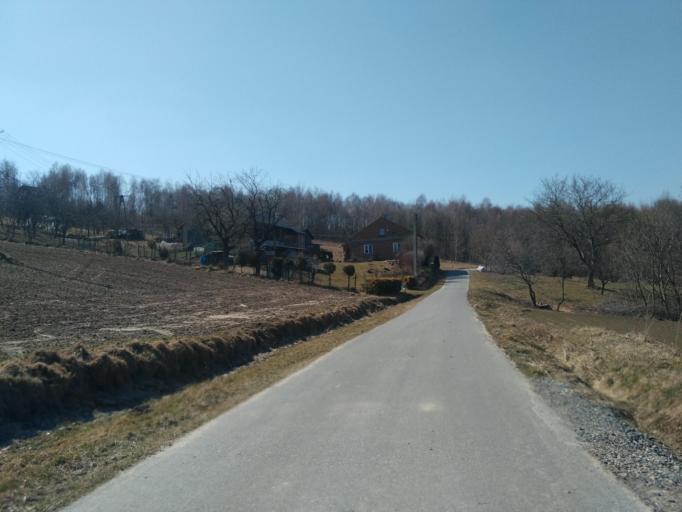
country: PL
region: Subcarpathian Voivodeship
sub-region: Powiat rzeszowski
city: Zglobien
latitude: 49.9862
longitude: 21.8356
